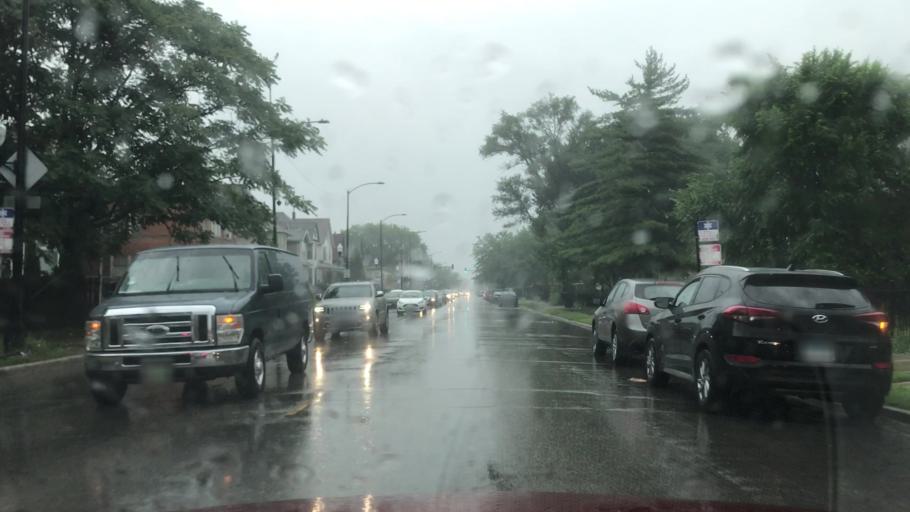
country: US
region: Illinois
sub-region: Cook County
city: Oak Park
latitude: 41.8896
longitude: -87.7554
